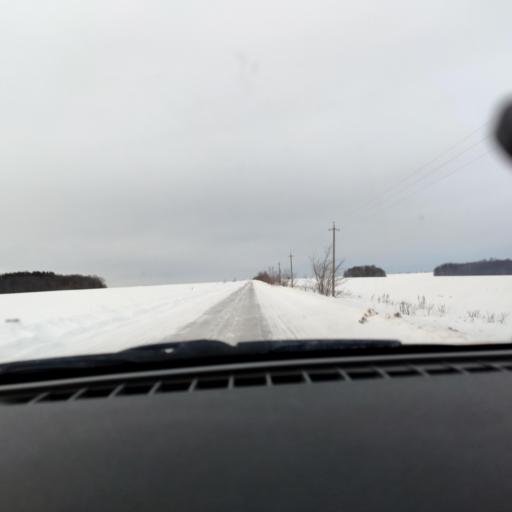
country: RU
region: Bashkortostan
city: Iglino
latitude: 54.7431
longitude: 56.5350
